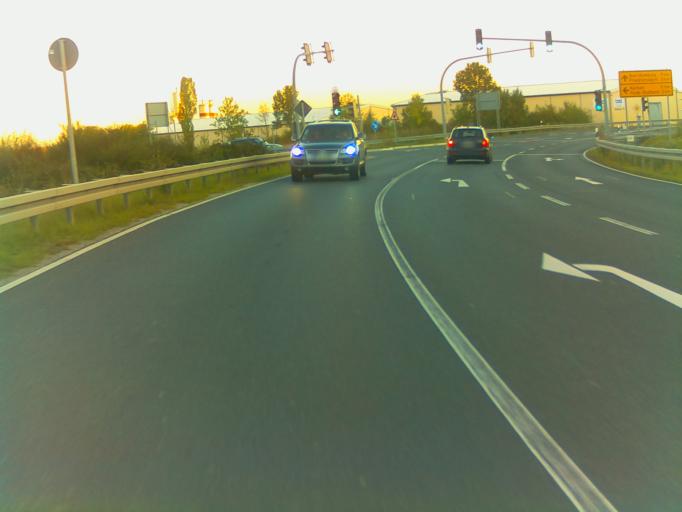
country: DE
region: Hesse
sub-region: Regierungsbezirk Darmstadt
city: Friedrichsdorf
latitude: 50.2732
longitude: 8.6685
